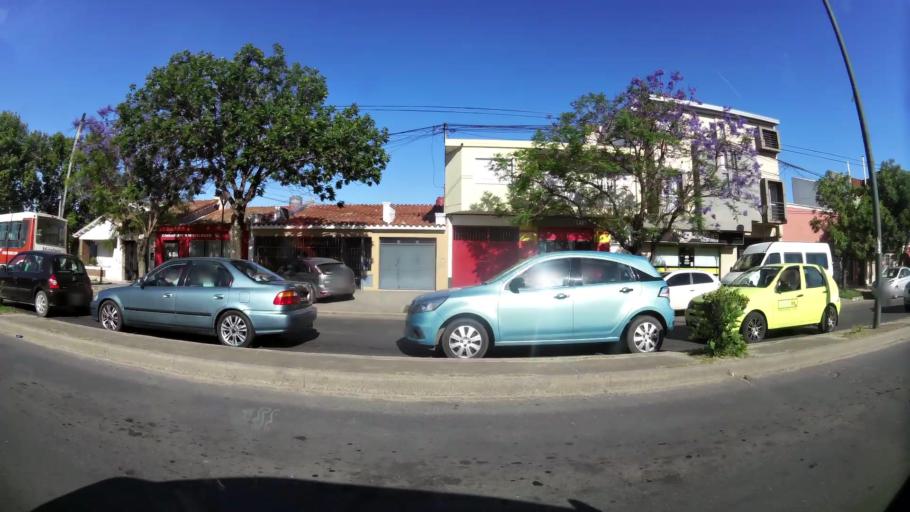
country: AR
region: Santa Fe
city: Santa Fe de la Vera Cruz
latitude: -31.6136
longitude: -60.7052
